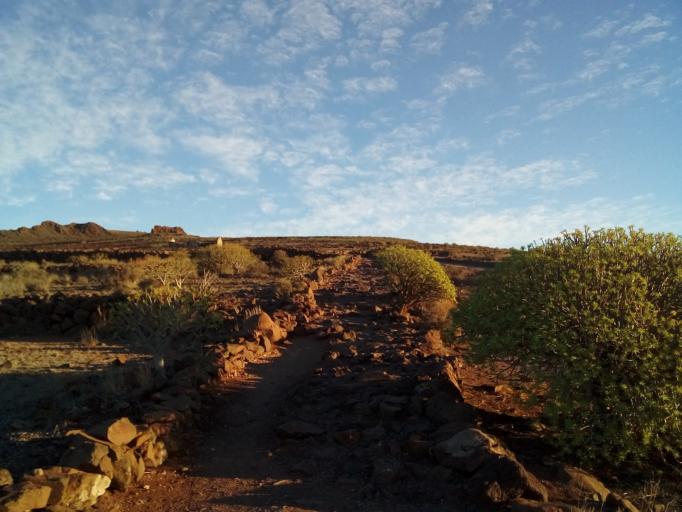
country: ES
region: Canary Islands
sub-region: Provincia de Santa Cruz de Tenerife
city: Vallehermosa
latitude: 28.1059
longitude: -17.3372
